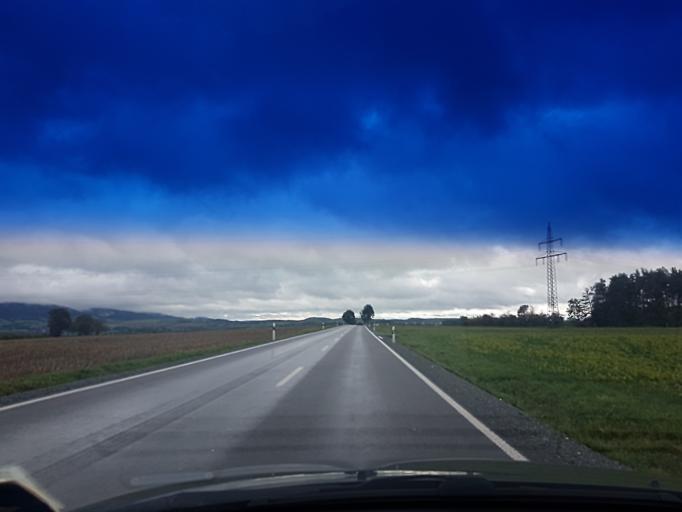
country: DE
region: Bavaria
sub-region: Upper Franconia
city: Bindlach
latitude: 50.0135
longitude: 11.6113
